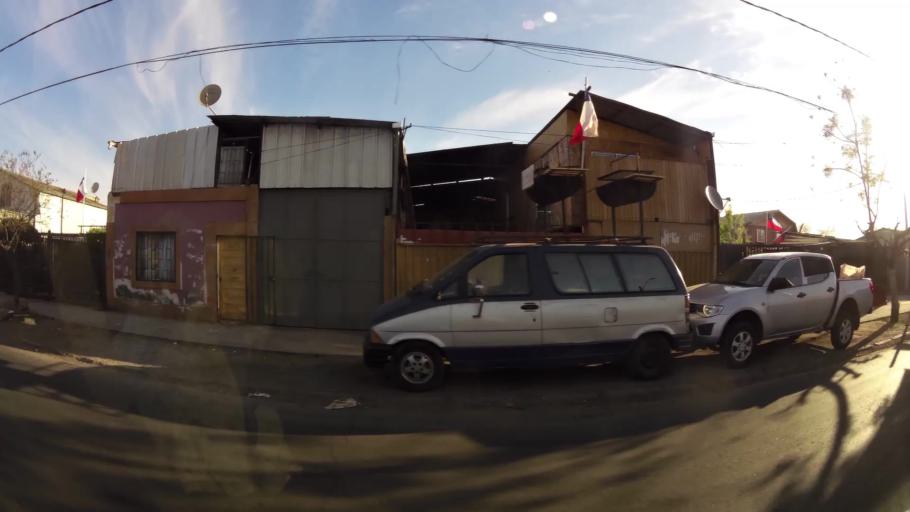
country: CL
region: Santiago Metropolitan
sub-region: Provincia de Santiago
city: Lo Prado
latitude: -33.4370
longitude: -70.7276
